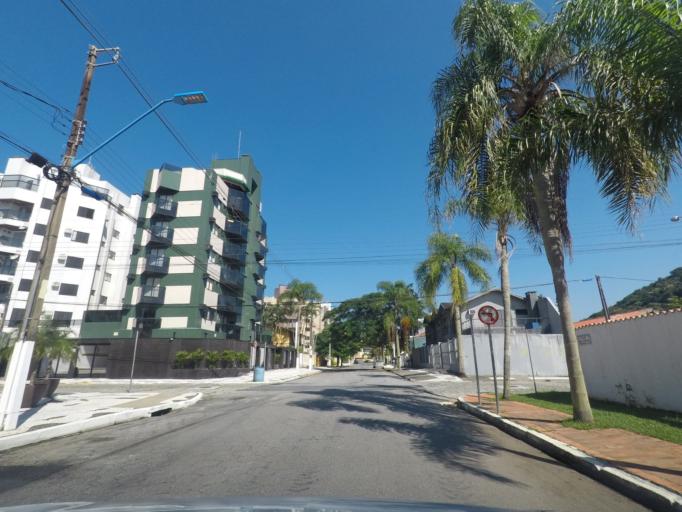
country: BR
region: Parana
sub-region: Guaratuba
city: Guaratuba
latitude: -25.8434
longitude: -48.5416
